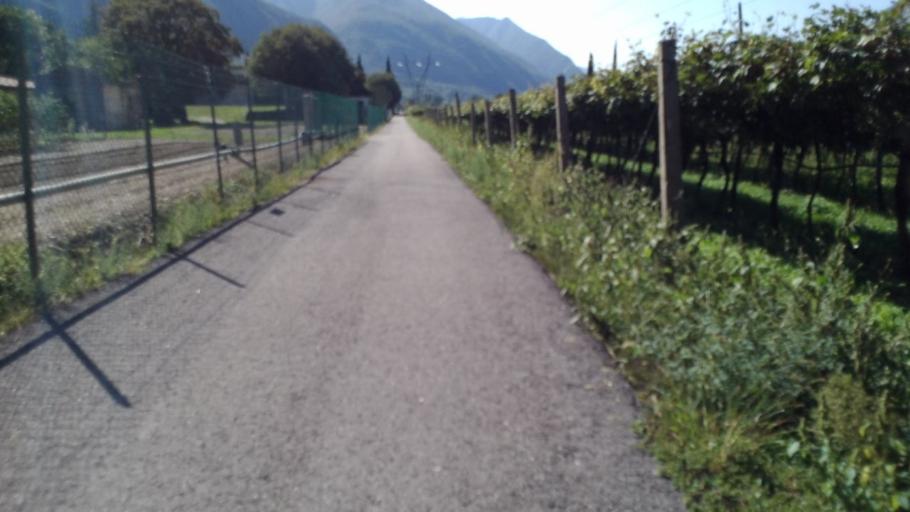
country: IT
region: Veneto
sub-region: Provincia di Verona
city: Brentino Belluno
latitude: 45.6586
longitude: 10.8987
